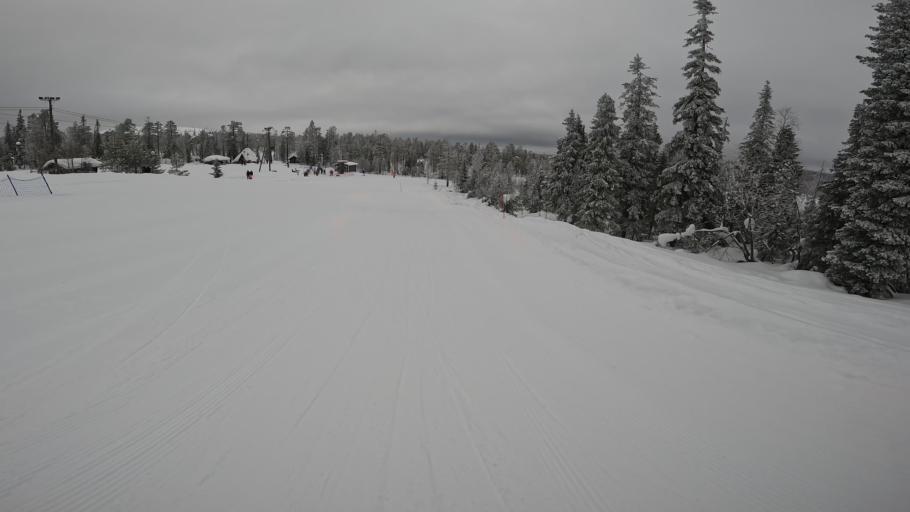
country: FI
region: Lapland
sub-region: Itae-Lappi
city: Salla
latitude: 66.7655
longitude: 28.7989
